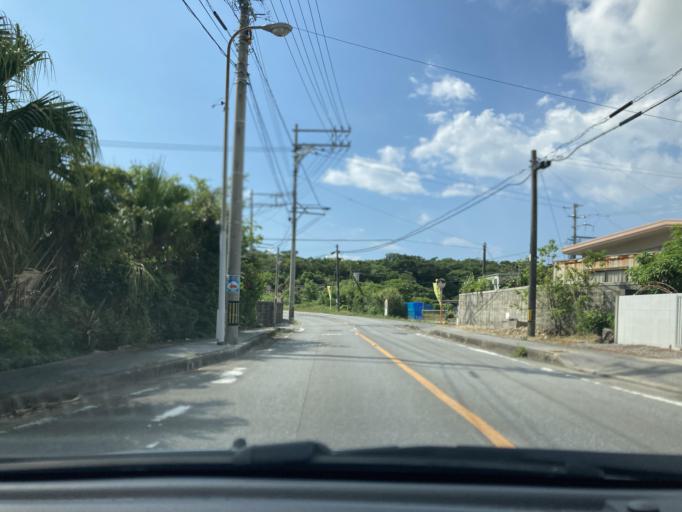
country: JP
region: Okinawa
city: Tomigusuku
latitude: 26.1489
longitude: 127.7910
